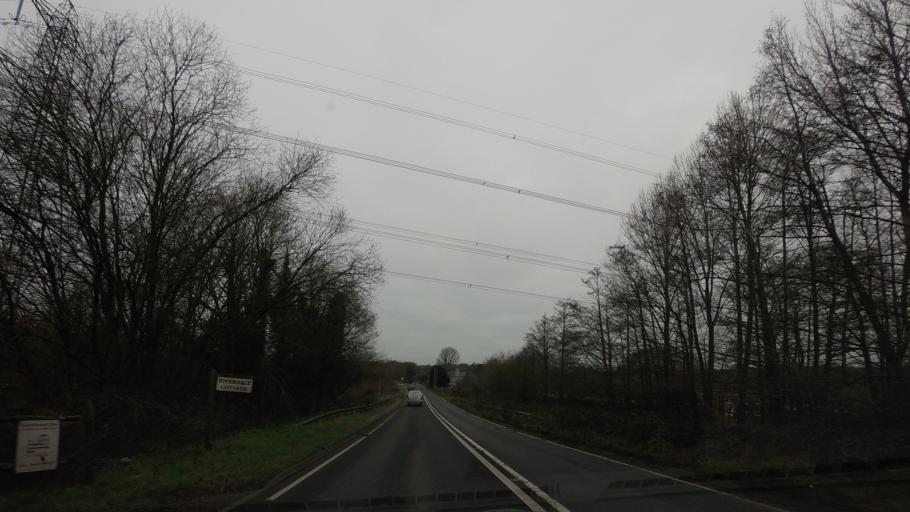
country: GB
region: England
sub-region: East Sussex
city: Saint Leonards-on-Sea
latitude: 50.9131
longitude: 0.5427
